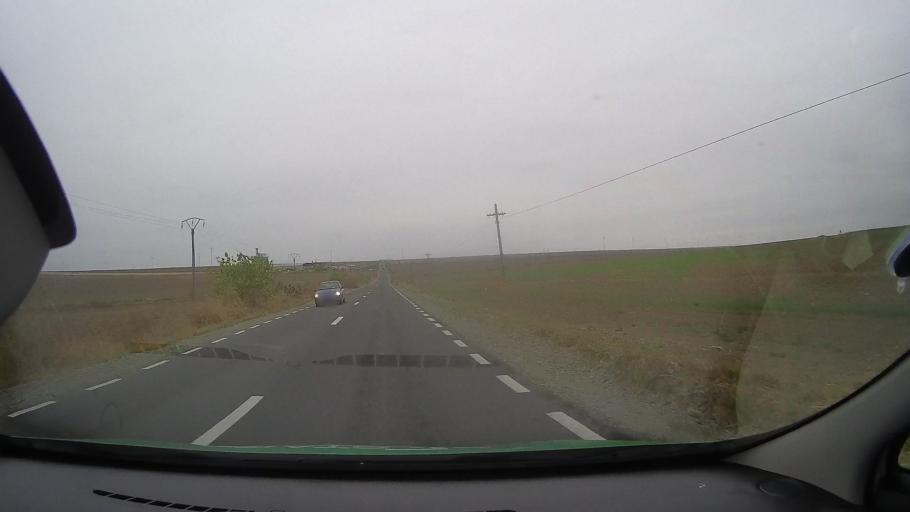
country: RO
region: Constanta
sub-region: Comuna Tortoman
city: Tortoman
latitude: 44.3593
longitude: 28.2107
